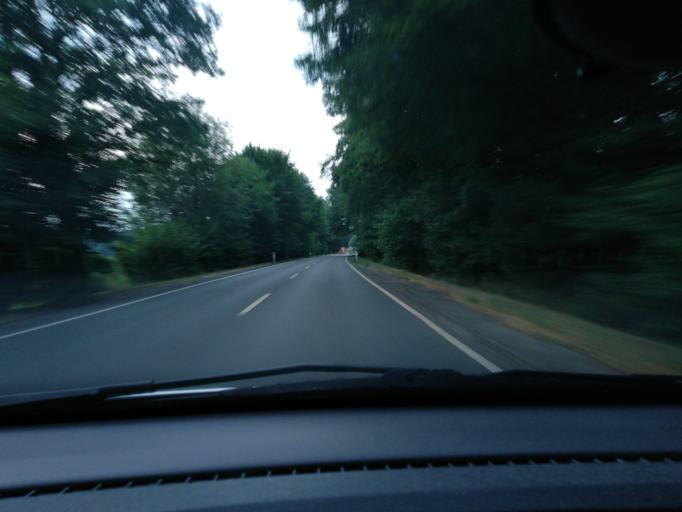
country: DE
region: North Rhine-Westphalia
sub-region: Regierungsbezirk Arnsberg
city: Schwelm
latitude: 51.3017
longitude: 7.2770
